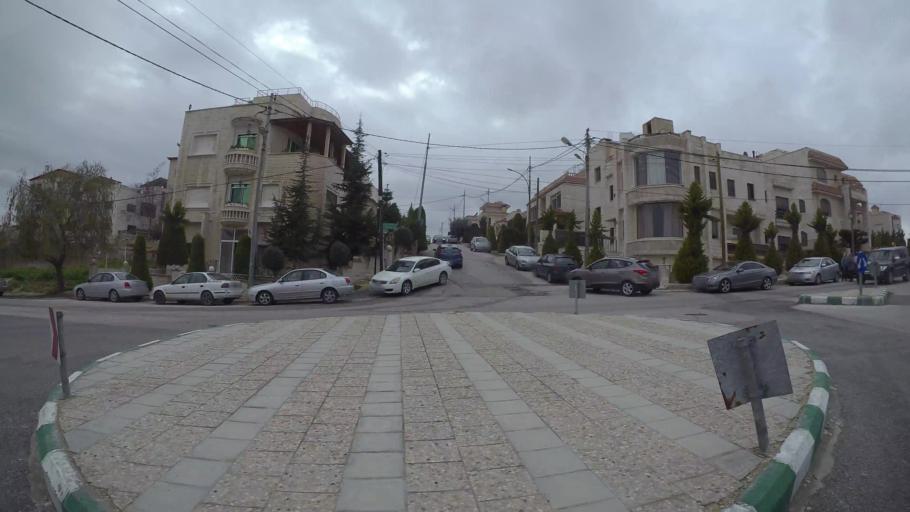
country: JO
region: Amman
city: Wadi as Sir
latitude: 31.9849
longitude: 35.8358
